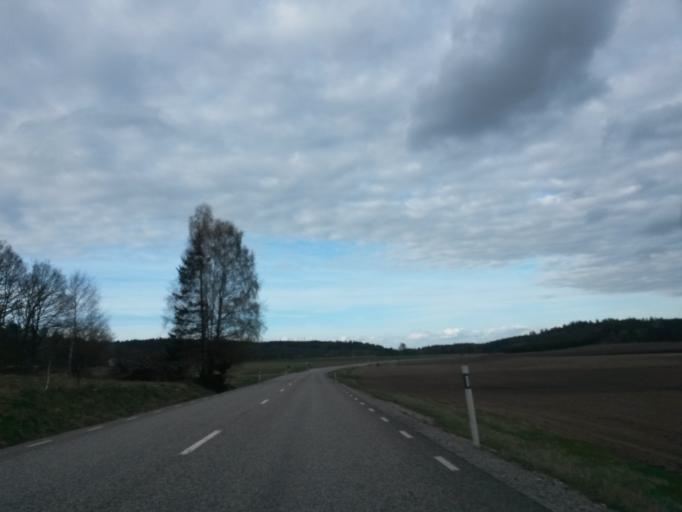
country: SE
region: Vaestra Goetaland
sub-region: Vargarda Kommun
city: Jonstorp
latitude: 58.0544
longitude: 12.6612
